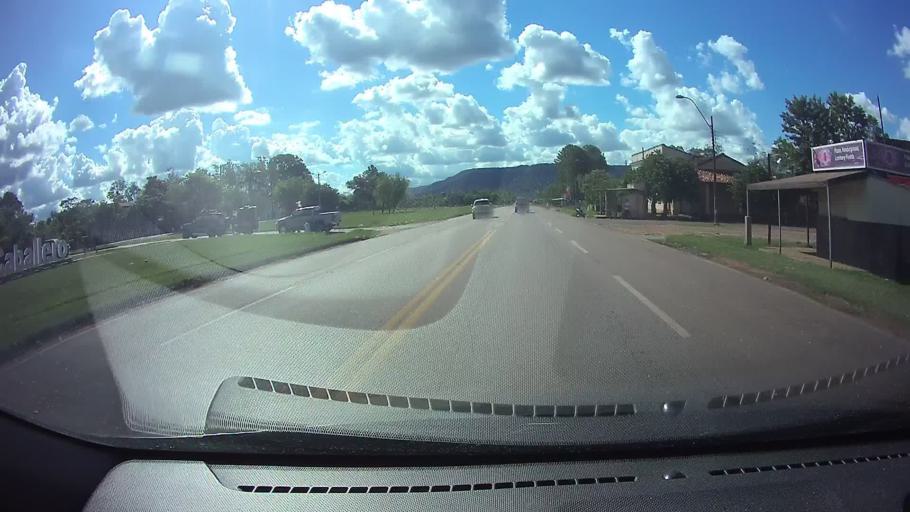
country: PY
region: Paraguari
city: Sapucai
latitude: -25.6915
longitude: -56.8625
